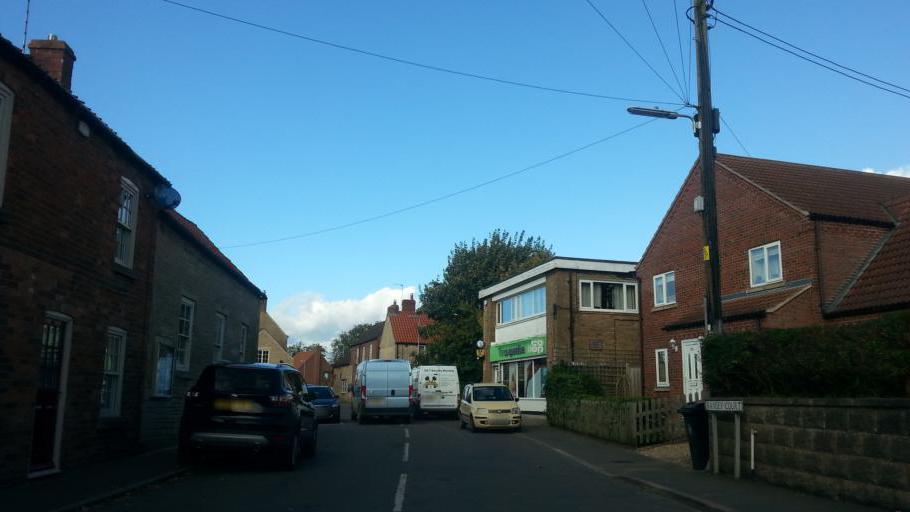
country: GB
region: England
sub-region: District of Rutland
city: Greetham
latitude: 52.8059
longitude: -0.6210
